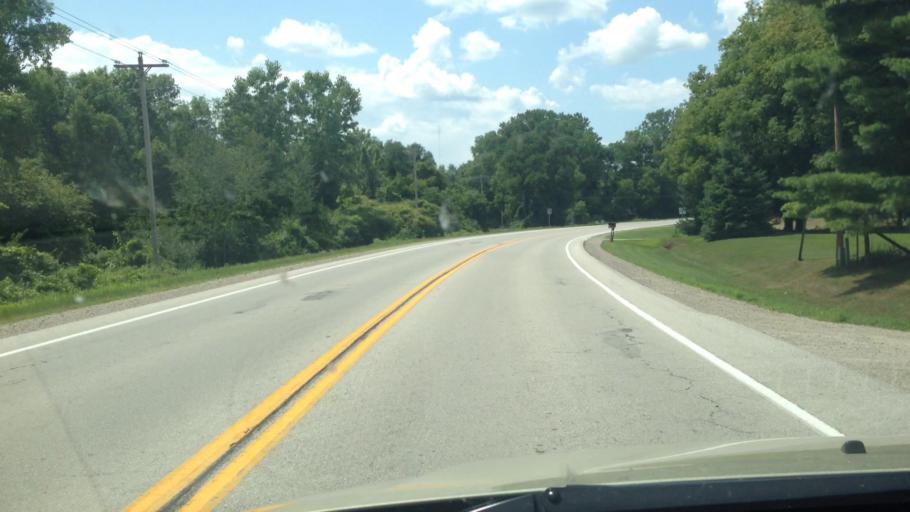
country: US
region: Wisconsin
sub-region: Brown County
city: Suamico
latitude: 44.6468
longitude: -88.1155
